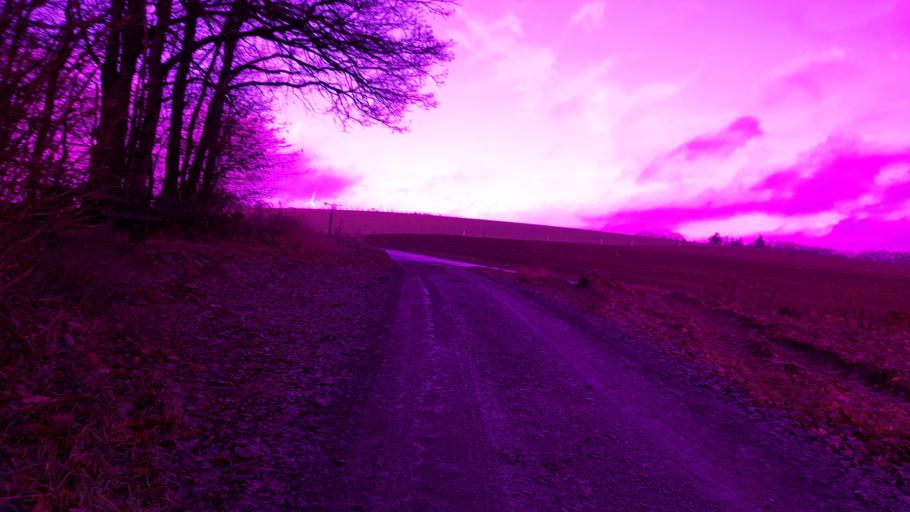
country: DE
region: Rheinland-Pfalz
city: Dasburg
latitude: 50.0890
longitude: 6.0978
